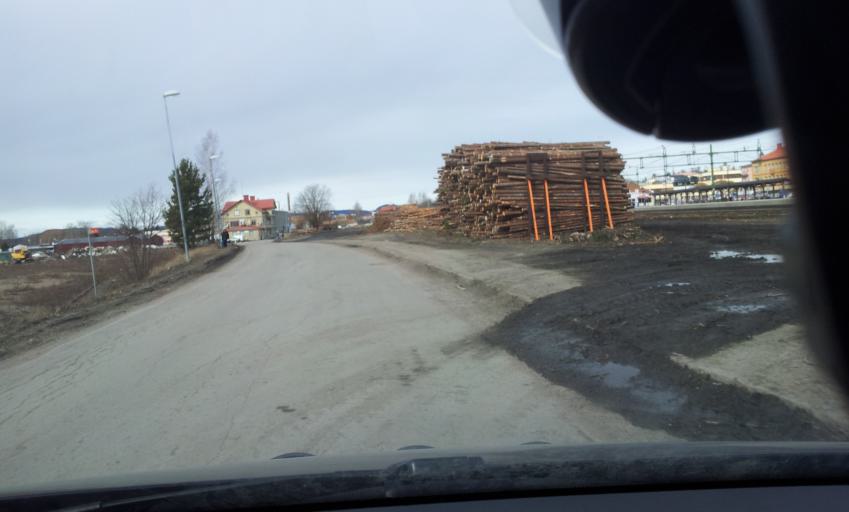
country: SE
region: Gaevleborg
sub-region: Ljusdals Kommun
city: Ljusdal
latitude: 61.8254
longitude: 16.1006
